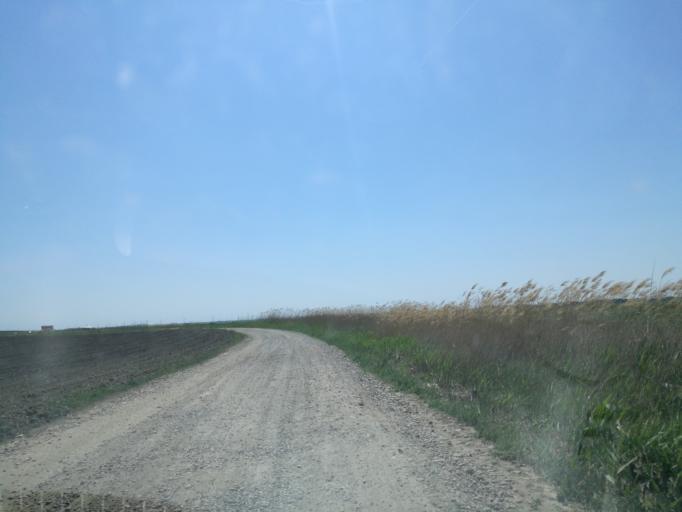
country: RO
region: Ialomita
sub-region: Comuna Adancata
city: Adancata
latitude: 44.7839
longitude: 26.4641
